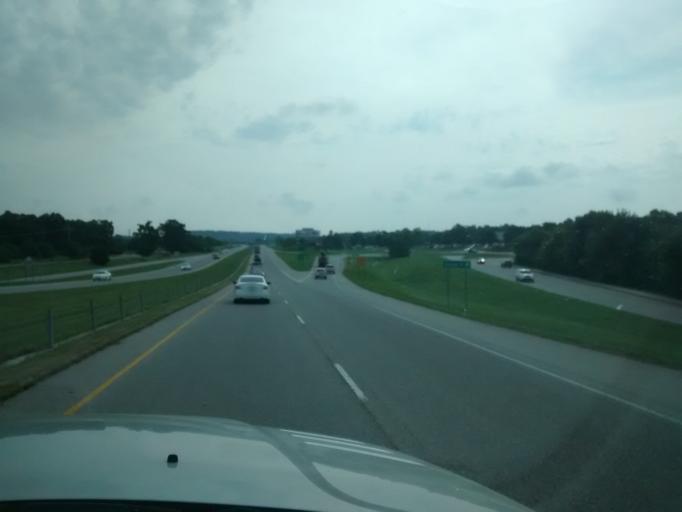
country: US
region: Arkansas
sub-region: Washington County
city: Johnson
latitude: 36.1119
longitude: -94.1619
